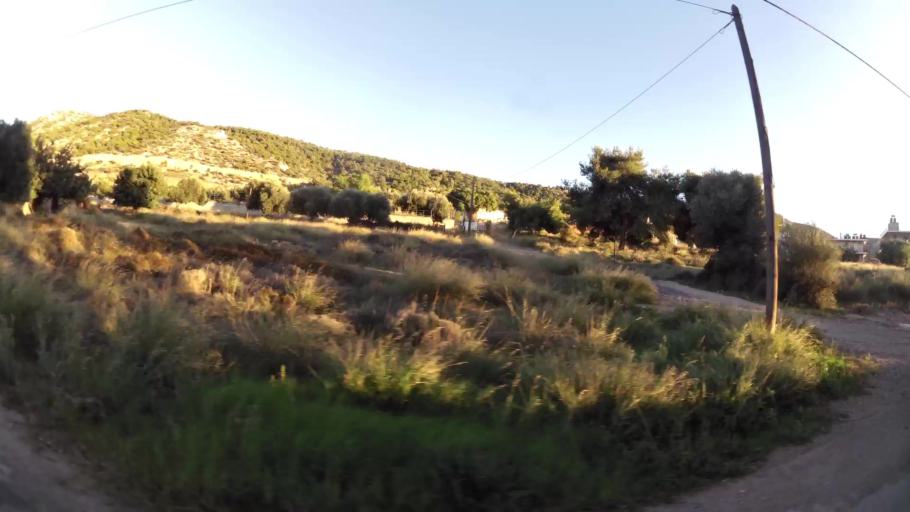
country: GR
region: Attica
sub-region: Nomarchia Athinas
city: Chaidari
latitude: 38.0411
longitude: 23.6380
